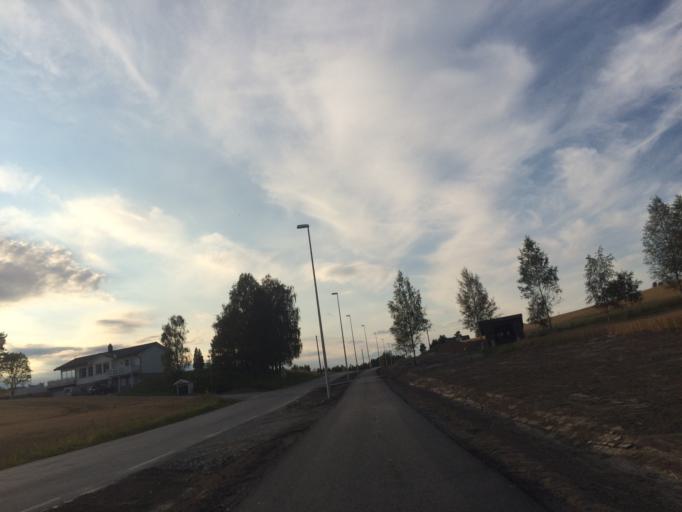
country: NO
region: Akershus
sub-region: Ski
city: Ski
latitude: 59.6889
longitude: 10.8652
